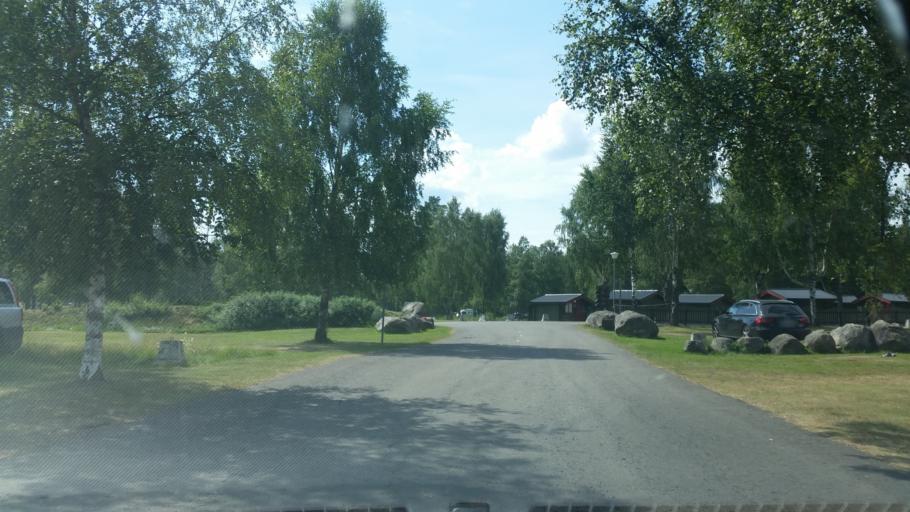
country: SE
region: Vaestra Goetaland
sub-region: Skara Kommun
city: Axvall
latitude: 58.4144
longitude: 13.5533
